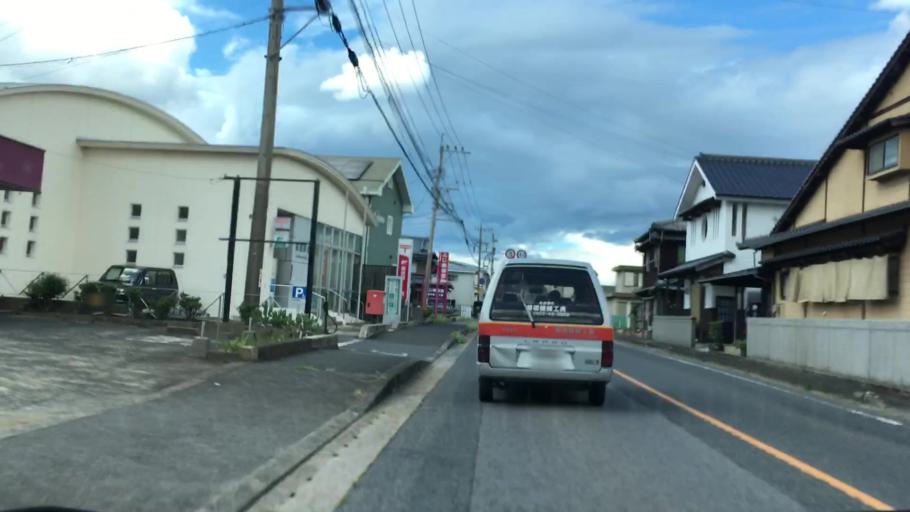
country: JP
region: Saga Prefecture
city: Imaricho-ko
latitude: 33.2020
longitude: 129.8502
